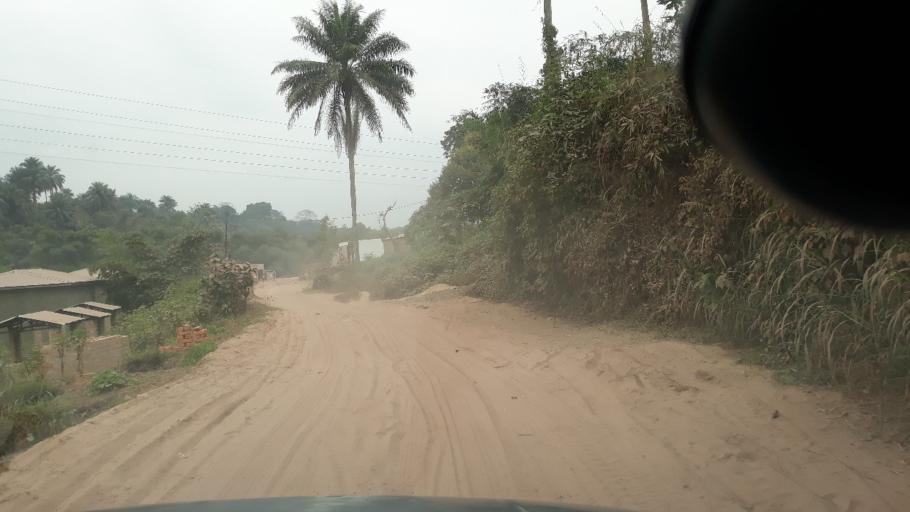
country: CD
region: Kinshasa
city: Masina
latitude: -4.4762
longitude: 15.2761
